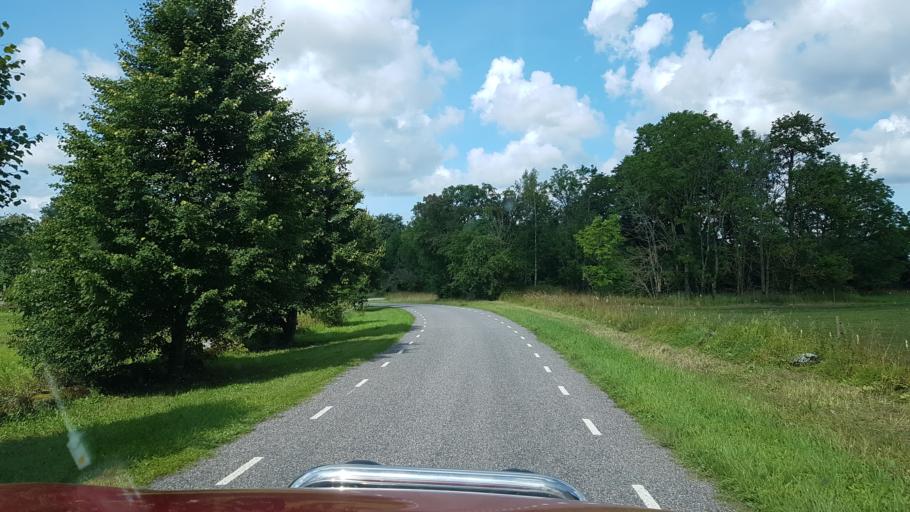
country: EE
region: Raplamaa
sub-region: Rapla vald
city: Rapla
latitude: 58.9675
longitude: 24.6305
